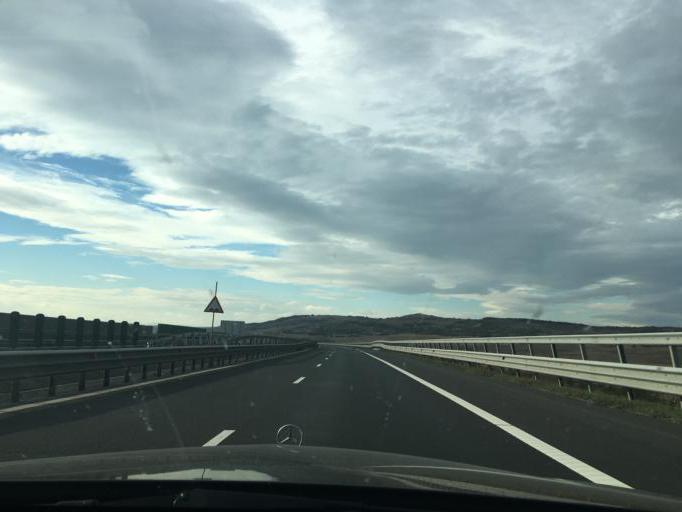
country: RO
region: Sibiu
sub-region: Comuna Apoldu de Jos
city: Apoldu de Jos
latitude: 45.8833
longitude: 23.8544
